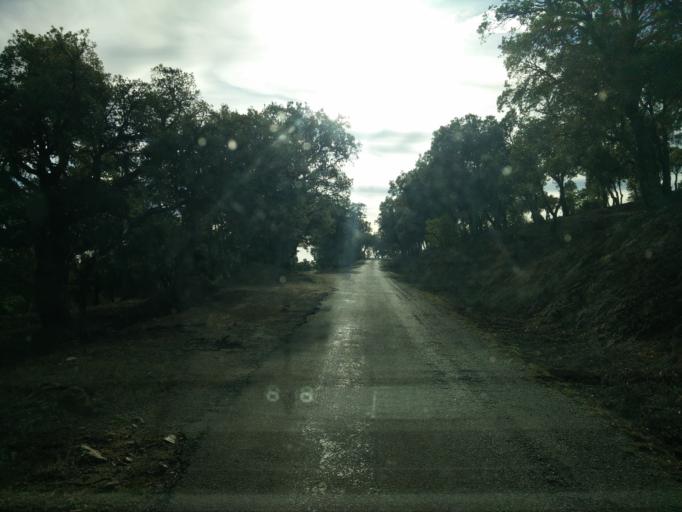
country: FR
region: Provence-Alpes-Cote d'Azur
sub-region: Departement du Var
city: Roquebrune-sur-Argens
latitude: 43.3986
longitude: 6.6346
